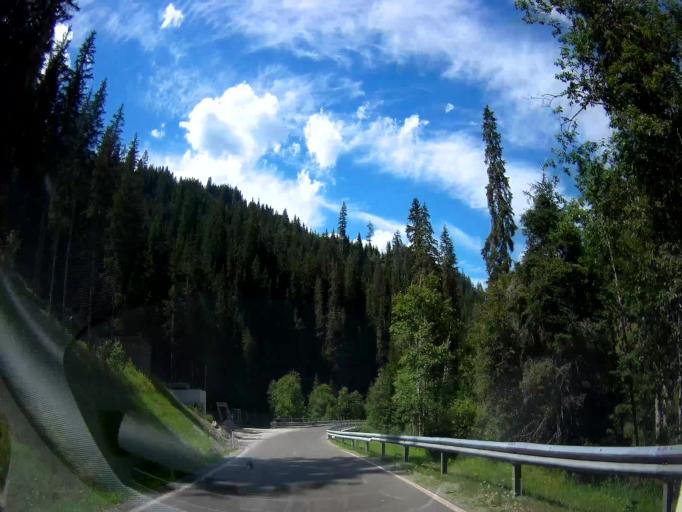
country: AT
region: Styria
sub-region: Politischer Bezirk Murau
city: Stadl an der Mur
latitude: 47.0232
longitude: 14.0062
